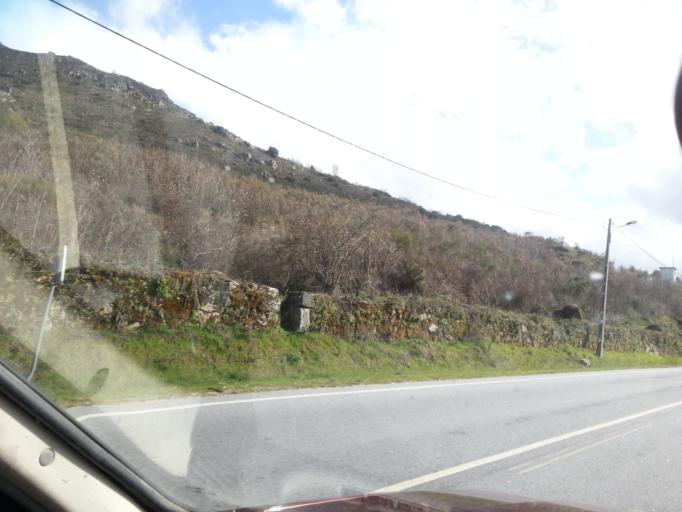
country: PT
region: Guarda
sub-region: Guarda
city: Guarda
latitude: 40.5777
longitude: -7.2954
